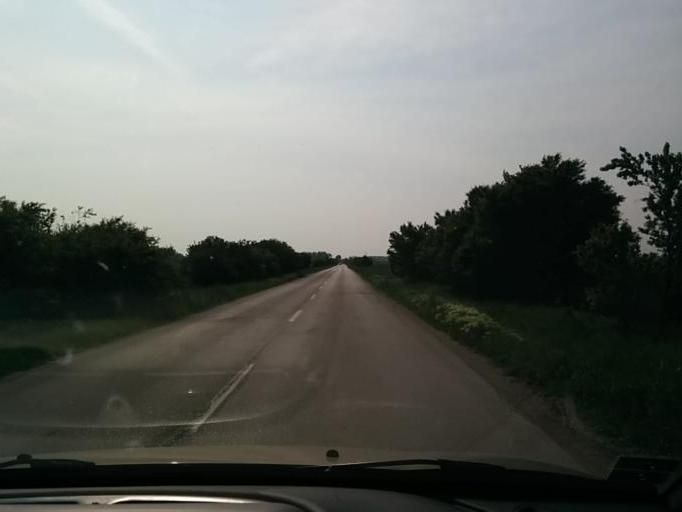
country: SK
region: Trnavsky
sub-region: Okres Galanta
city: Galanta
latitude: 48.2388
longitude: 17.7020
